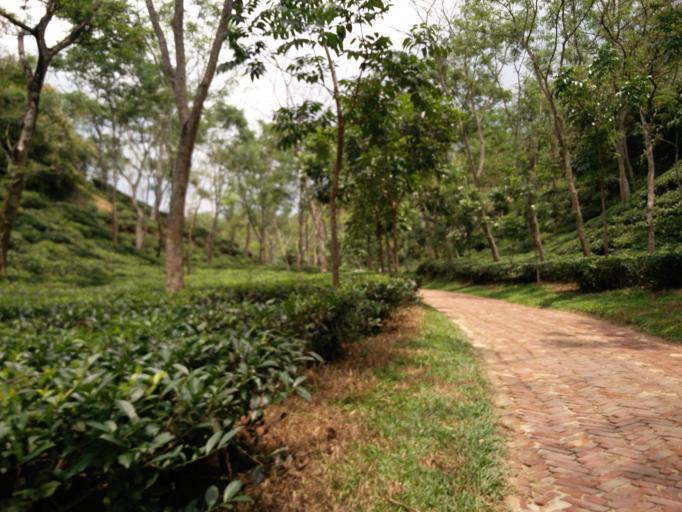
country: IN
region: Tripura
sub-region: Dhalai
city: Kamalpur
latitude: 24.3040
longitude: 91.8005
